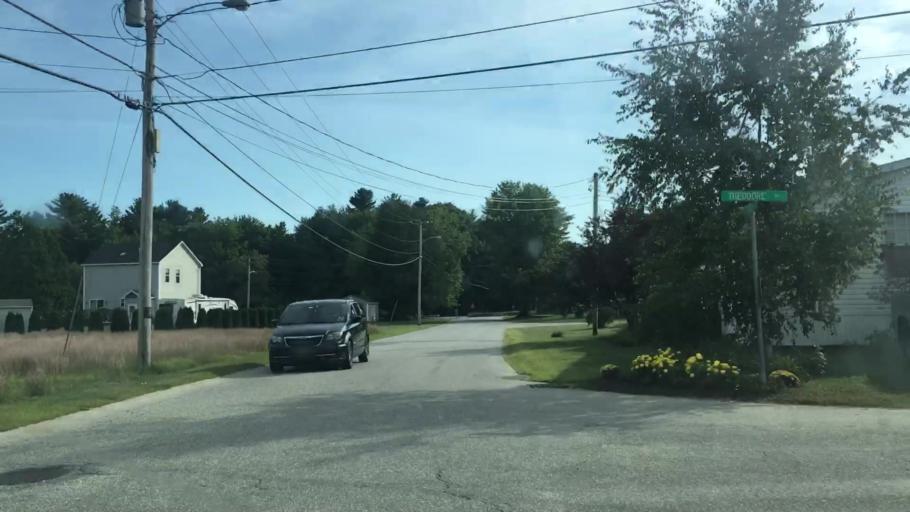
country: US
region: Maine
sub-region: Sagadahoc County
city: North Bath
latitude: 43.9343
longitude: -69.8746
